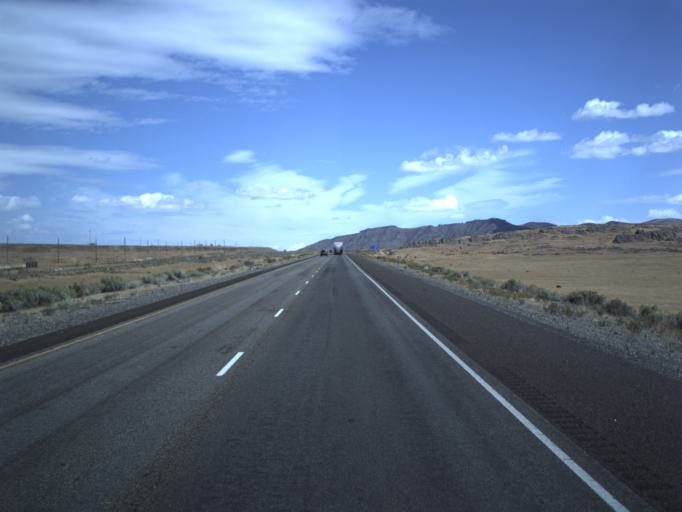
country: US
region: Utah
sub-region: Tooele County
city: Grantsville
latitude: 40.7545
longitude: -113.0299
